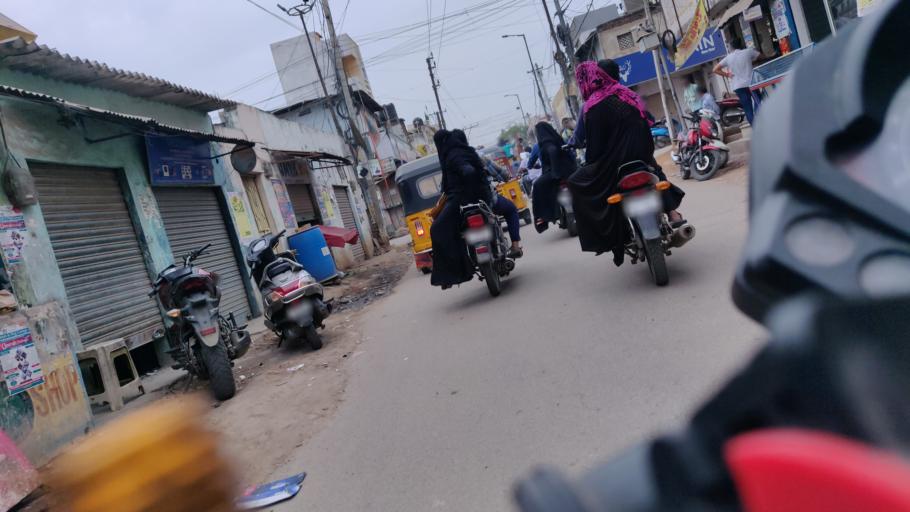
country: IN
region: Telangana
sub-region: Rangareddi
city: Kukatpalli
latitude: 17.4538
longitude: 78.4120
